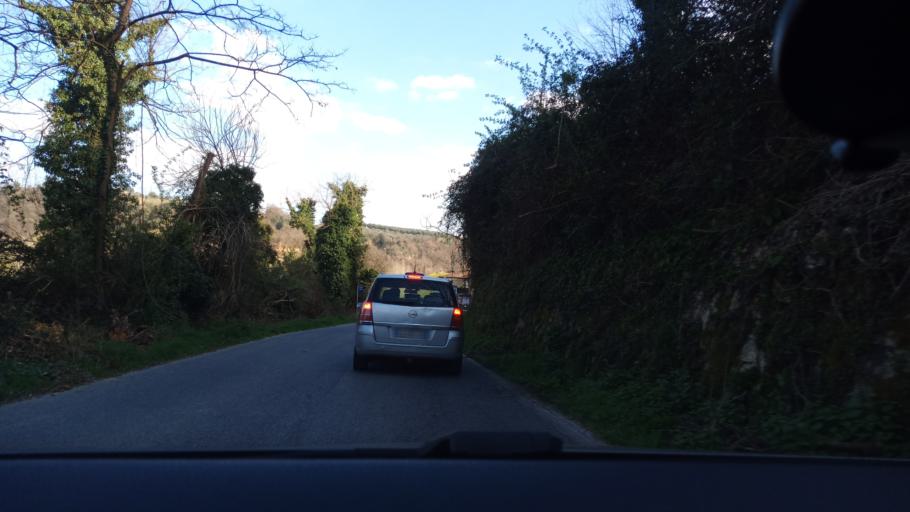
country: IT
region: Latium
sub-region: Citta metropolitana di Roma Capitale
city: Torrita Tiberina
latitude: 42.2363
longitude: 12.6260
